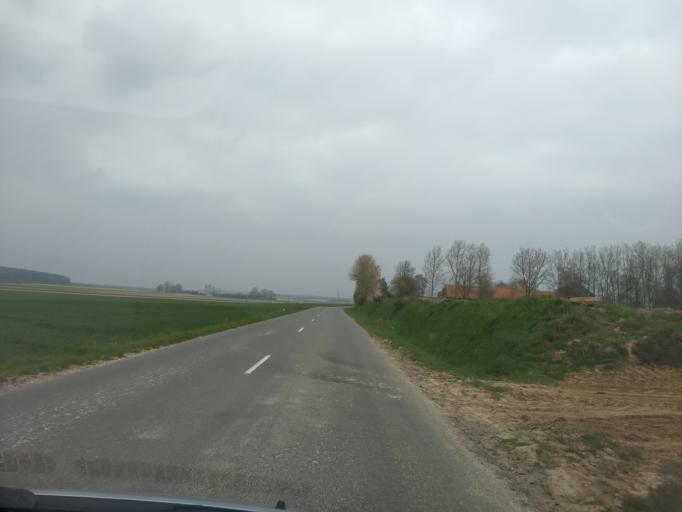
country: FR
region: Nord-Pas-de-Calais
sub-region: Departement du Pas-de-Calais
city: Mont-Saint-Eloi
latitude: 50.3475
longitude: 2.7039
